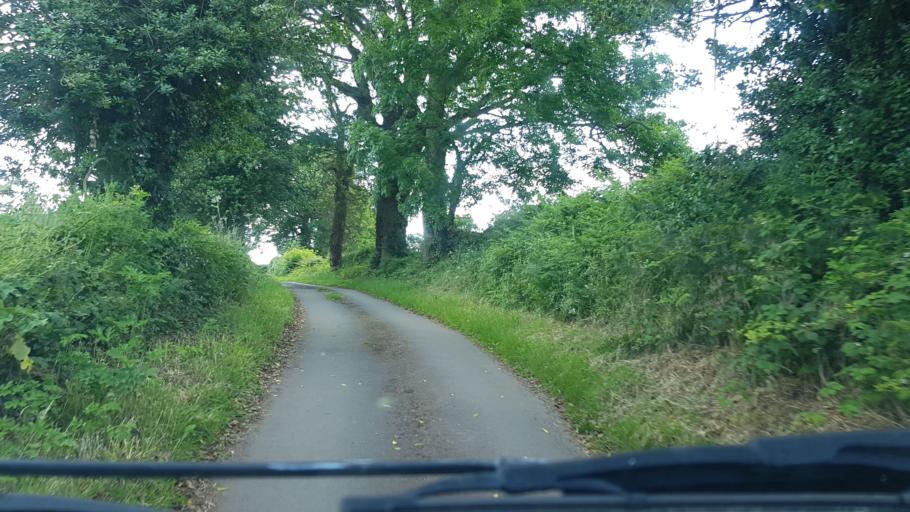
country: GB
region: England
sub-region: Shropshire
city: Romsley
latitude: 52.4640
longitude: -2.2666
